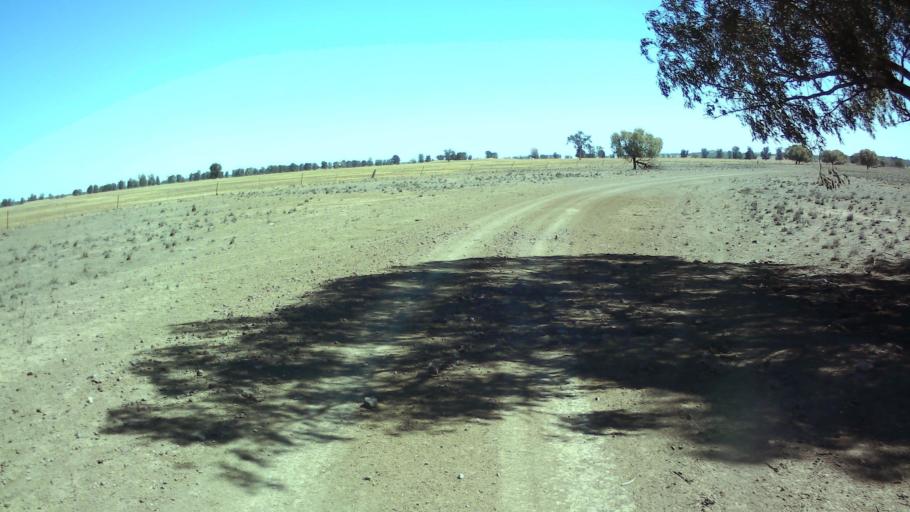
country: AU
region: New South Wales
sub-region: Forbes
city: Forbes
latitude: -33.7223
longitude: 147.6653
